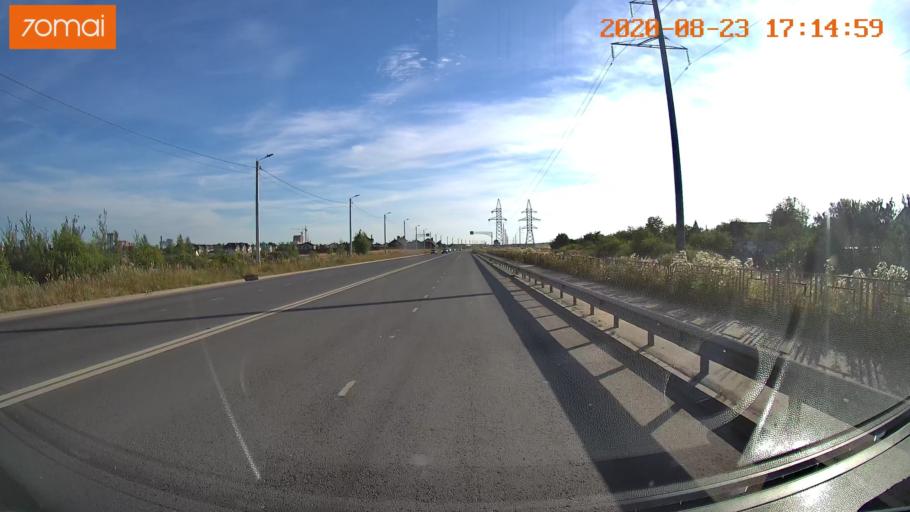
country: RU
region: Ivanovo
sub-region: Gorod Ivanovo
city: Ivanovo
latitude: 57.0487
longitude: 40.9184
